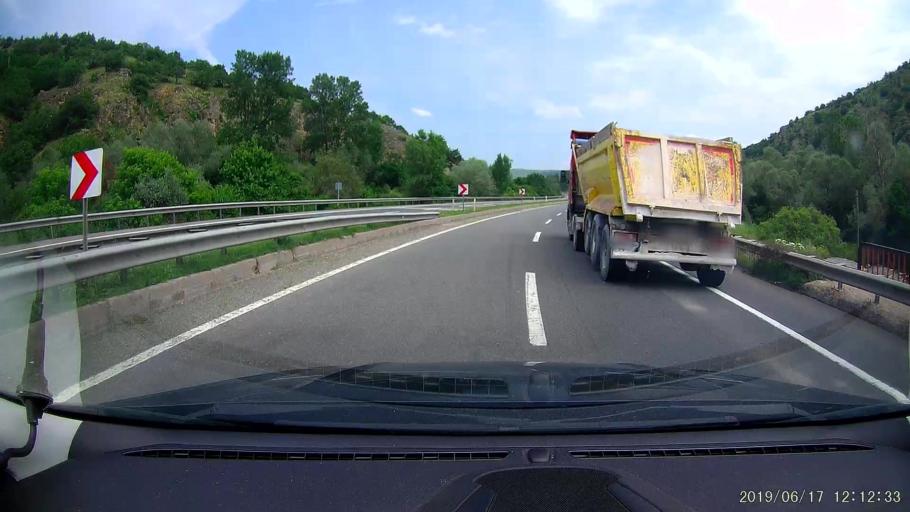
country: TR
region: Karabuk
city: Gozyeri
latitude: 40.8582
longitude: 32.6362
